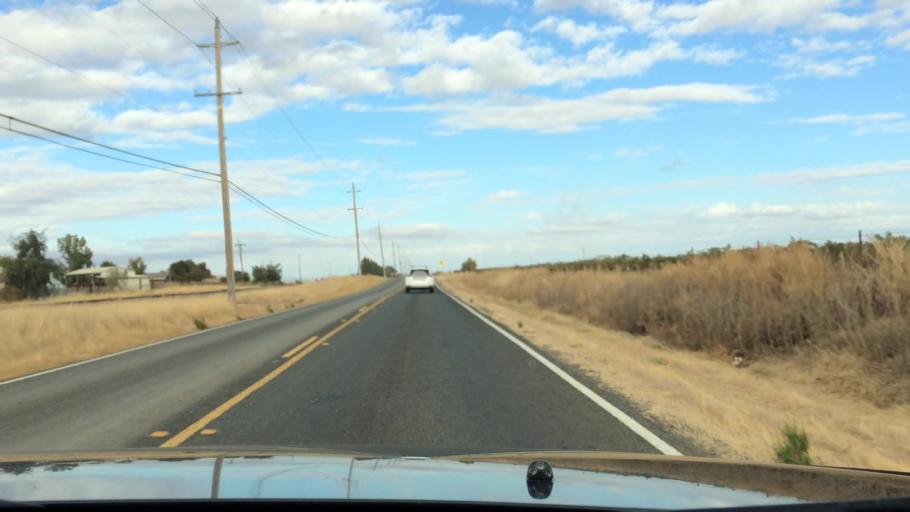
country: US
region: California
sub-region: Sacramento County
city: Clay
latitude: 38.3194
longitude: -121.2016
